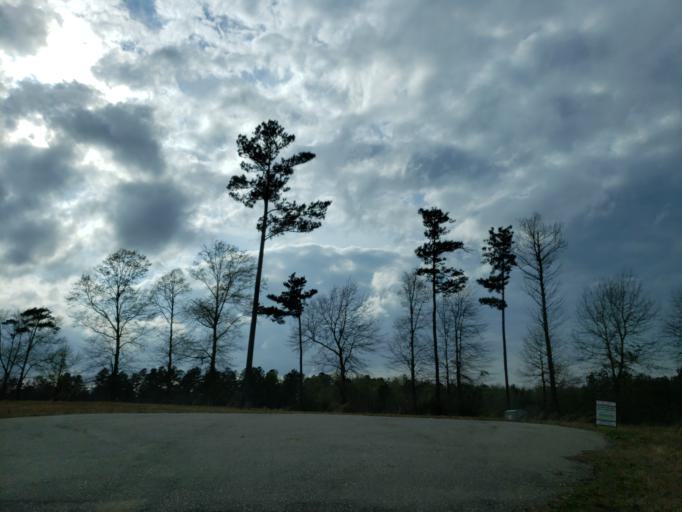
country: US
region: Mississippi
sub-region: Jones County
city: Ellisville
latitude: 31.5596
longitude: -89.2563
